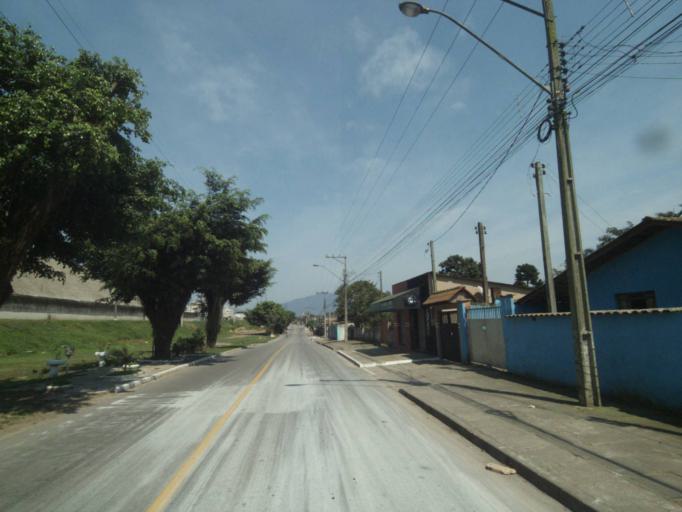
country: BR
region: Parana
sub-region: Paranagua
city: Paranagua
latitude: -25.5384
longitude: -48.5411
